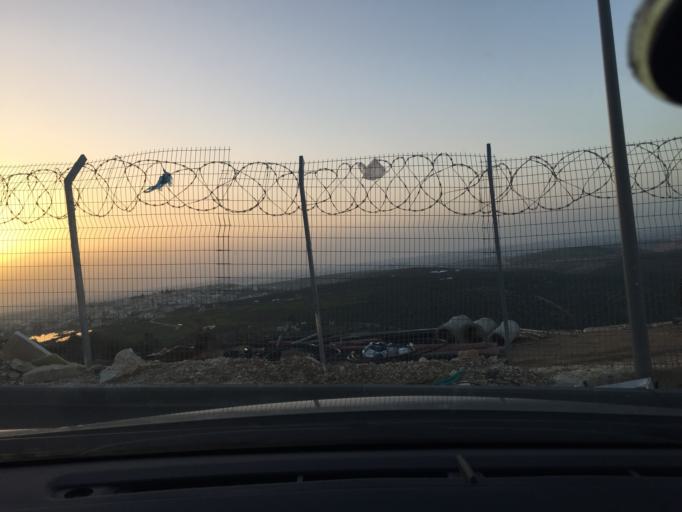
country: PS
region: West Bank
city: Rafat
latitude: 32.0675
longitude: 35.0454
